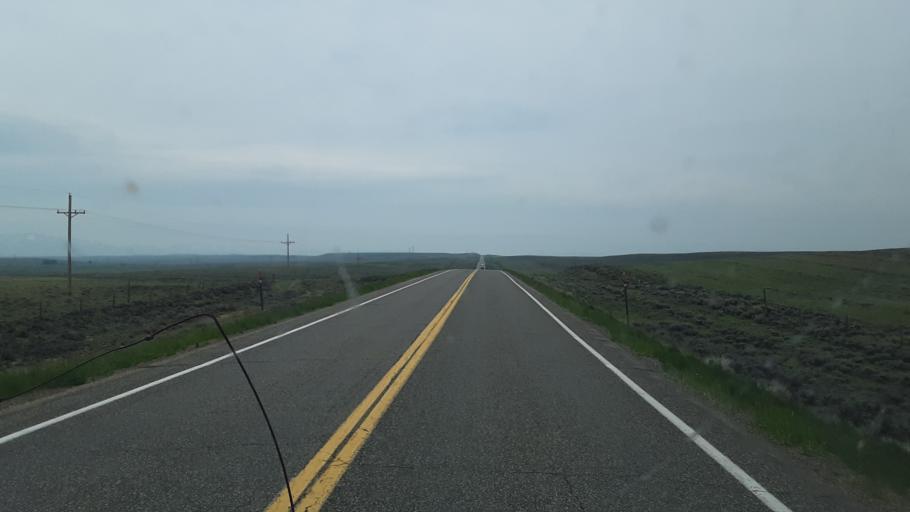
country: US
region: Colorado
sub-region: Jackson County
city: Walden
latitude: 40.8469
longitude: -106.3074
